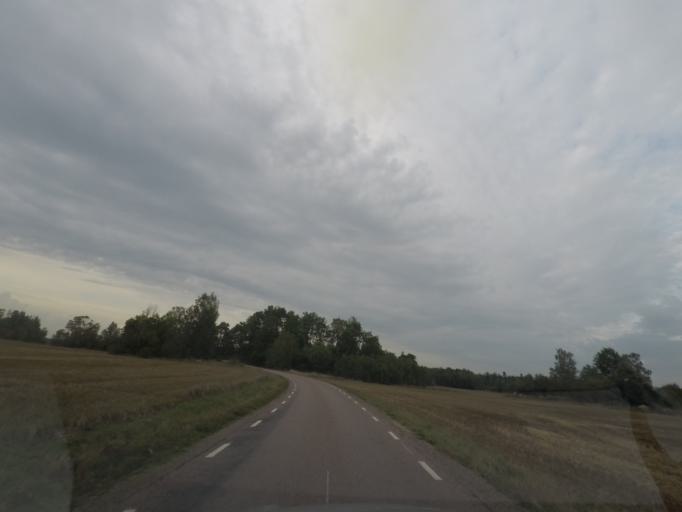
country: SE
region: Vaestmanland
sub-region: Hallstahammars Kommun
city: Kolback
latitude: 59.5161
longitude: 16.1887
